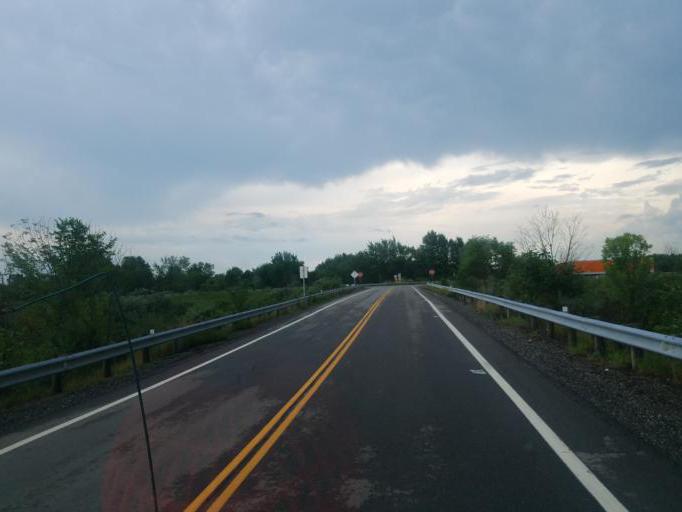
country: US
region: Ohio
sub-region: Wayne County
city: Doylestown
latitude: 40.9565
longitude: -81.7370
